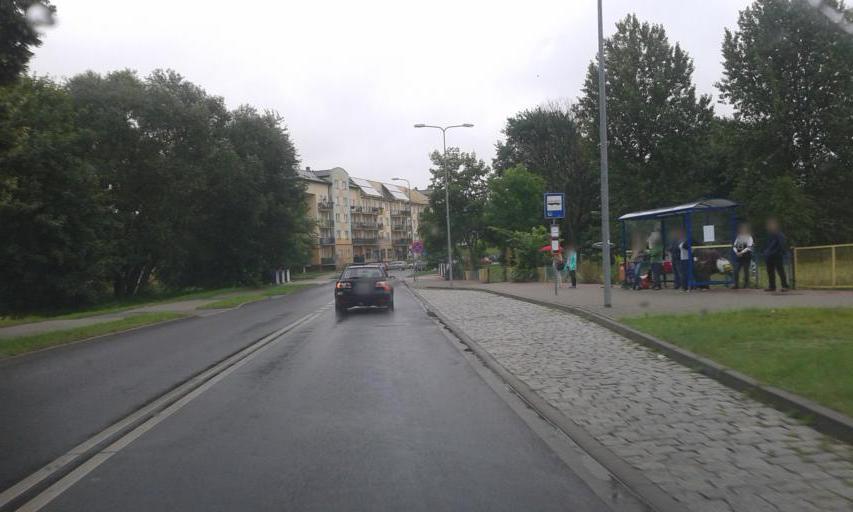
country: PL
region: West Pomeranian Voivodeship
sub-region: Powiat szczecinecki
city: Szczecinek
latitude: 53.7140
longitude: 16.6942
